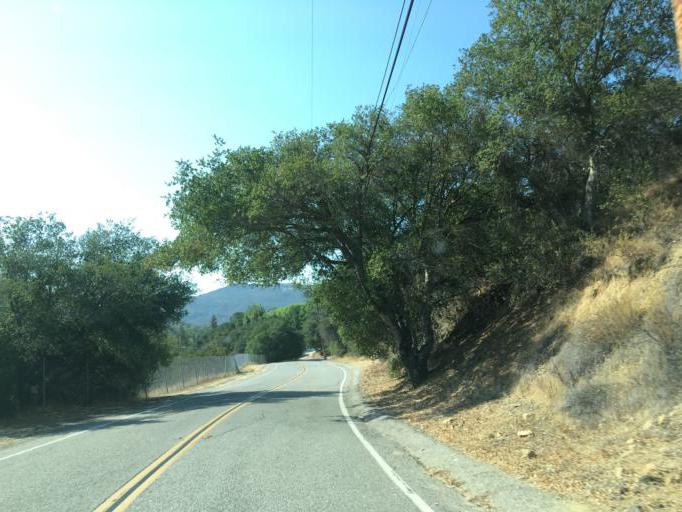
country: US
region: California
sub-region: Los Angeles County
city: Hidden Hills
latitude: 34.1207
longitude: -118.6619
